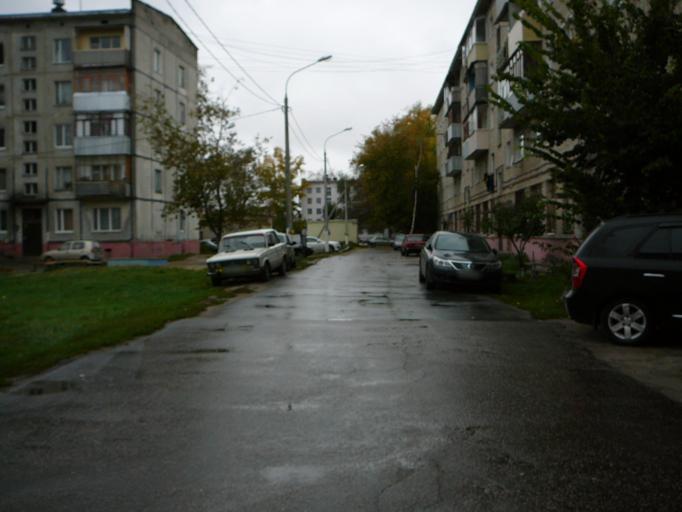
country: RU
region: Moskovskaya
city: Shatura
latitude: 55.5752
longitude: 39.5342
